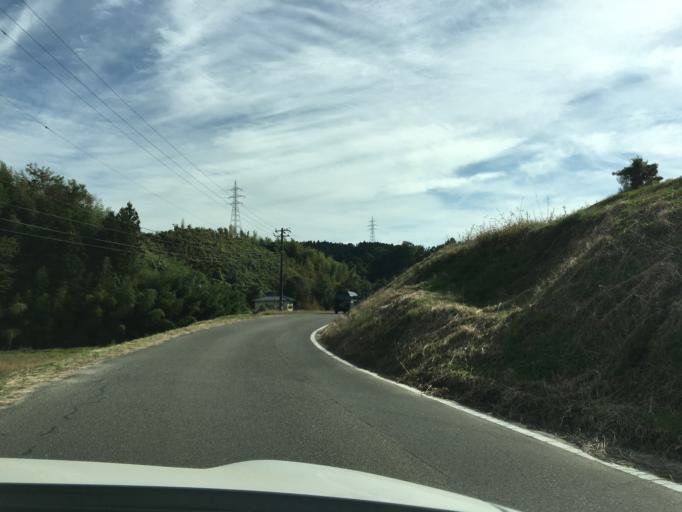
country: JP
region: Fukushima
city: Miharu
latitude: 37.5072
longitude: 140.5014
